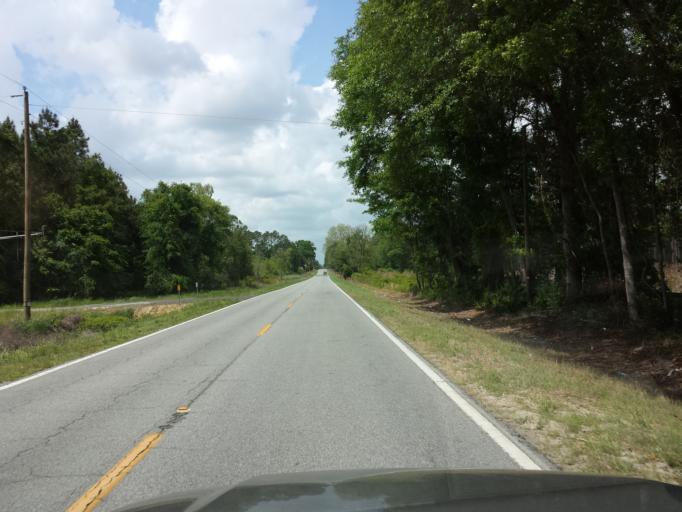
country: US
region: Georgia
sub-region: Echols County
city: Statenville
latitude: 30.6376
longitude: -83.1322
